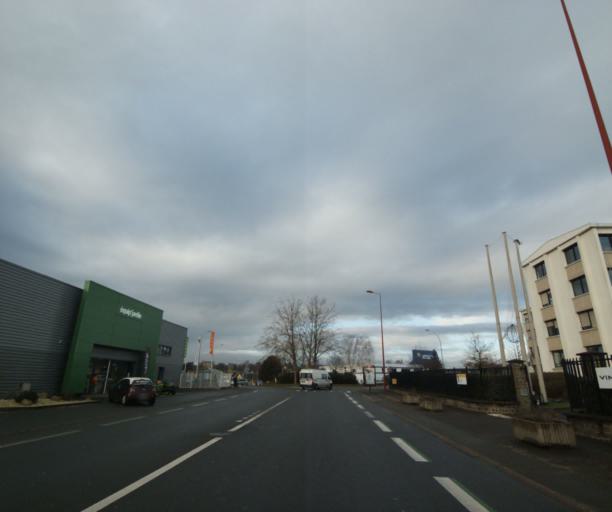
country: FR
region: Pays de la Loire
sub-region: Departement de la Sarthe
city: La Chapelle-Saint-Aubin
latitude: 48.0247
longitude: 0.1779
